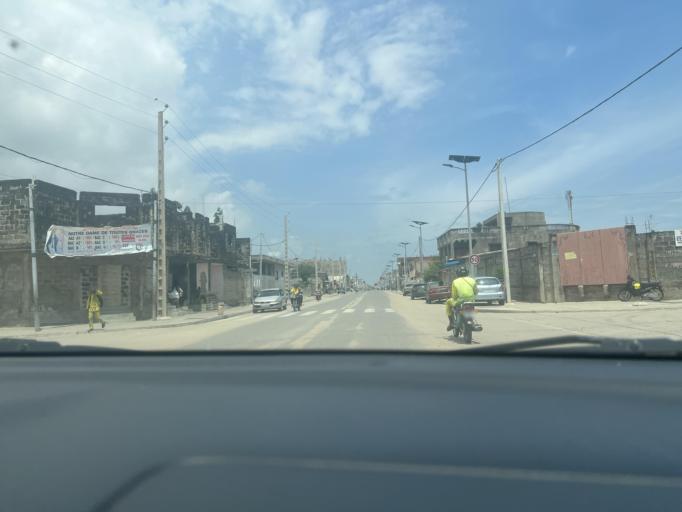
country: BJ
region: Littoral
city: Cotonou
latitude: 6.3859
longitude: 2.4534
